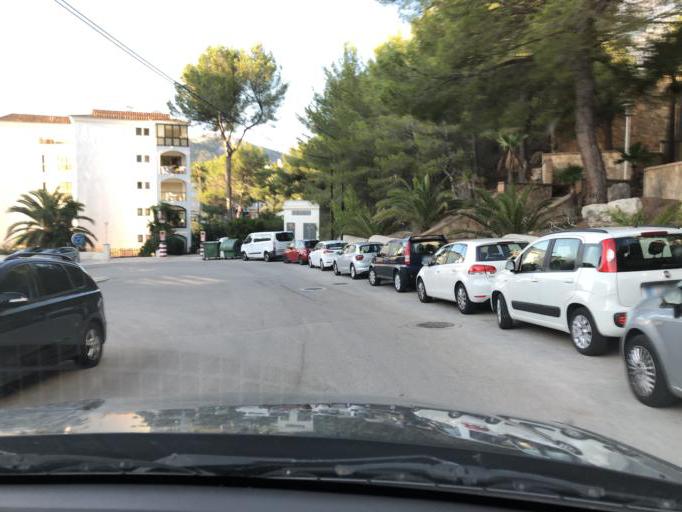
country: ES
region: Balearic Islands
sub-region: Illes Balears
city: Santa Ponsa
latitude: 39.5350
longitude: 2.4597
